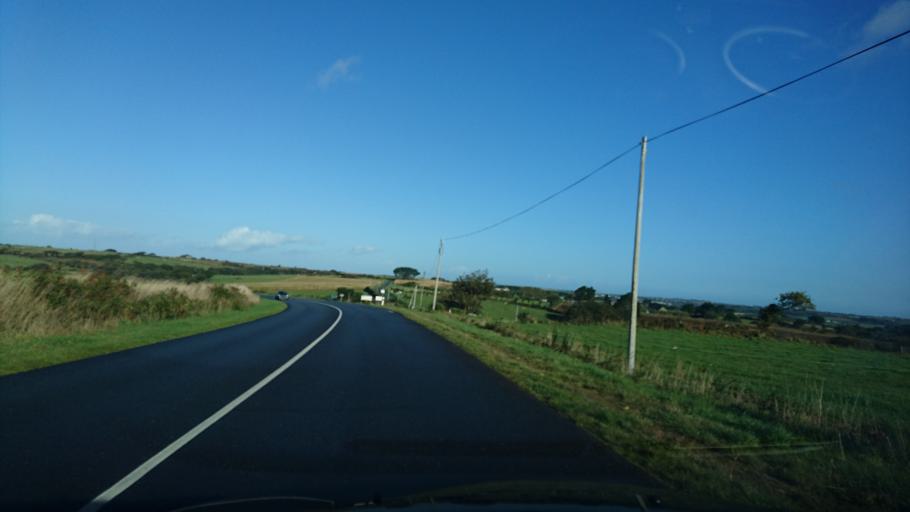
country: FR
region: Brittany
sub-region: Departement du Finistere
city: Plouarzel
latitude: 48.4367
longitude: -4.7158
